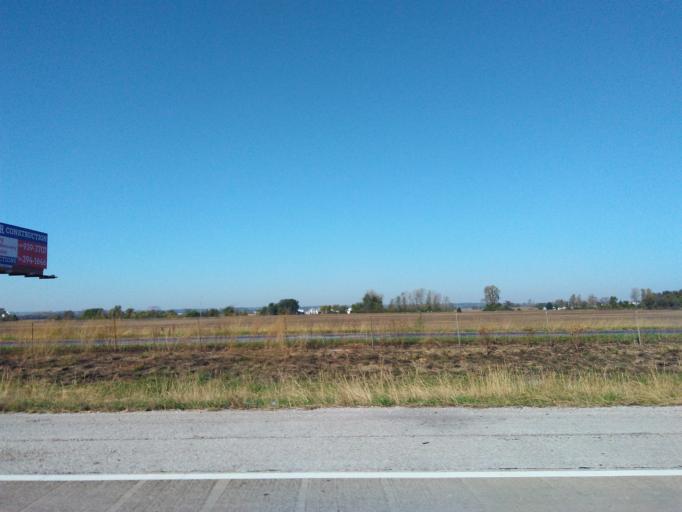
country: US
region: Illinois
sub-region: Saint Clair County
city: Dupo
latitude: 38.4867
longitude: -90.2199
